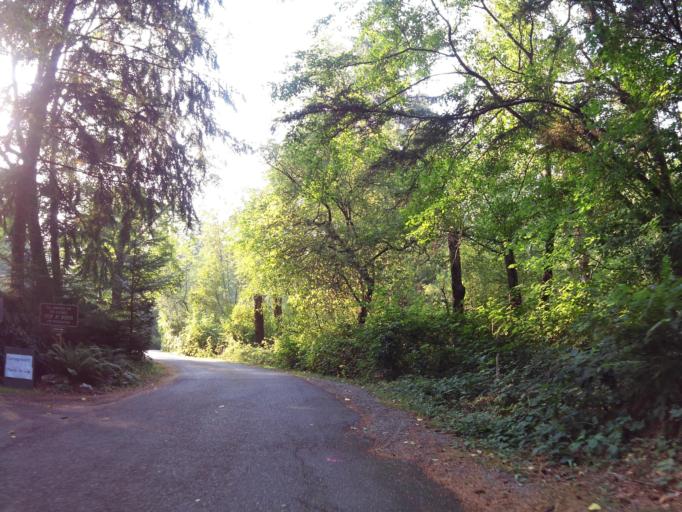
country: US
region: Washington
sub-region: Whatcom County
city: Birch Bay
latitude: 48.9034
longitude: -122.7600
